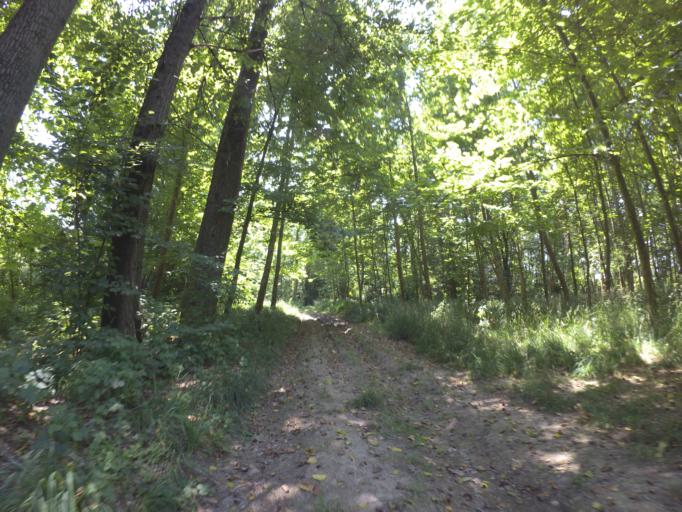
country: IT
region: Friuli Venezia Giulia
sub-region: Provincia di Udine
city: Rivignano
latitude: 45.8958
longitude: 13.0398
